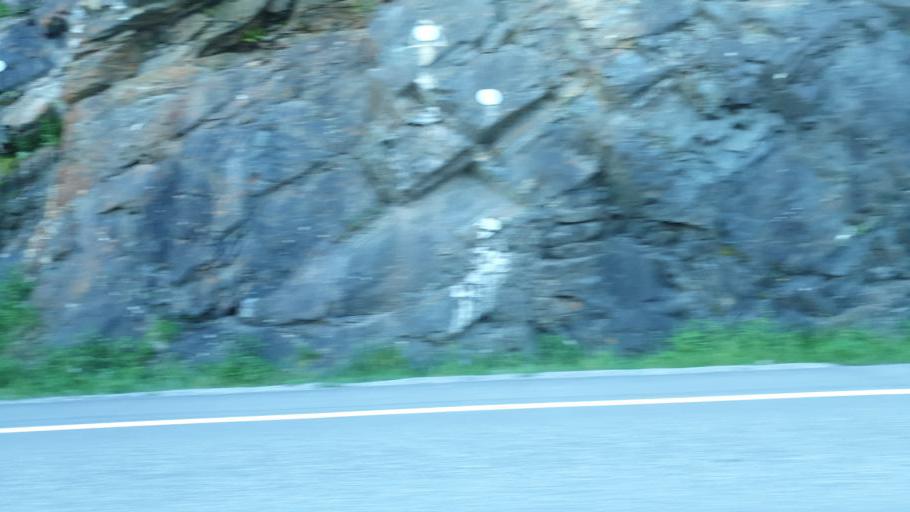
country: NO
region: Sor-Trondelag
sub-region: Rissa
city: Rissa
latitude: 63.5065
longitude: 10.1311
